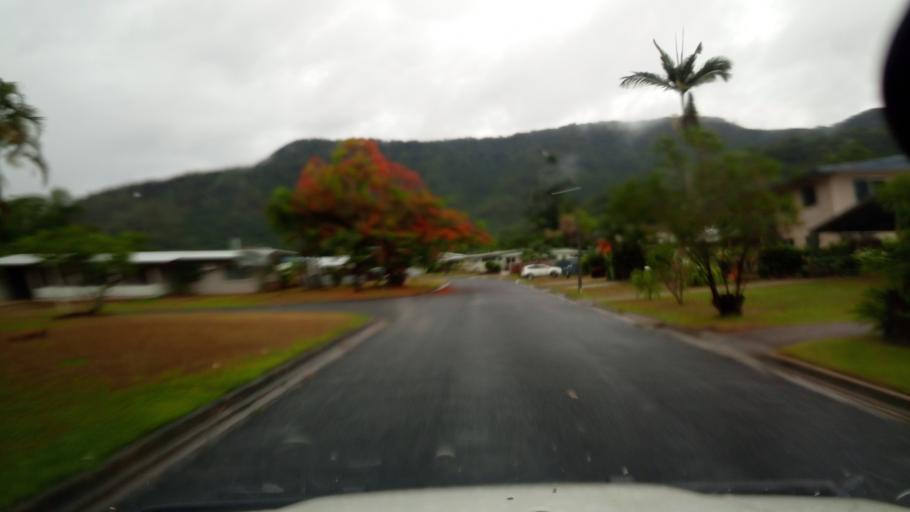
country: AU
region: Queensland
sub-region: Cairns
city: Woree
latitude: -16.9555
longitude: 145.7299
